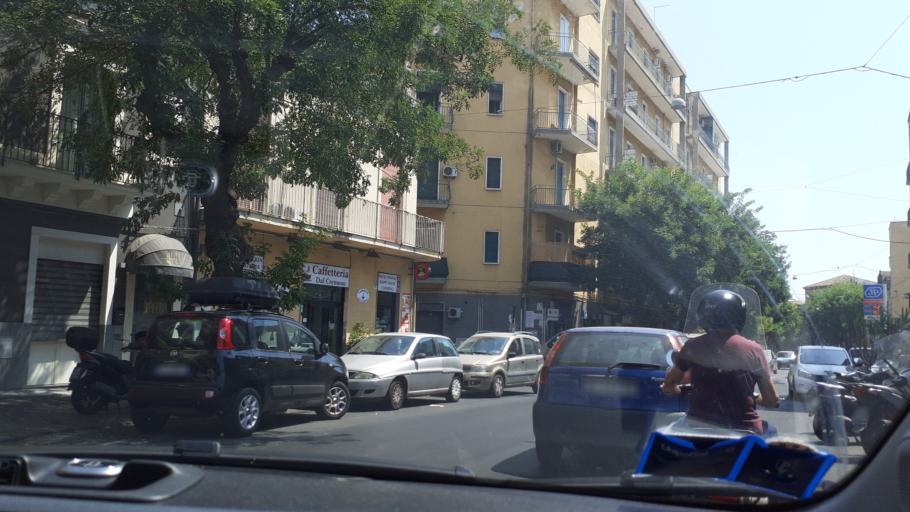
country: IT
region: Sicily
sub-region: Catania
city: Catania
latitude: 37.5075
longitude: 15.0799
